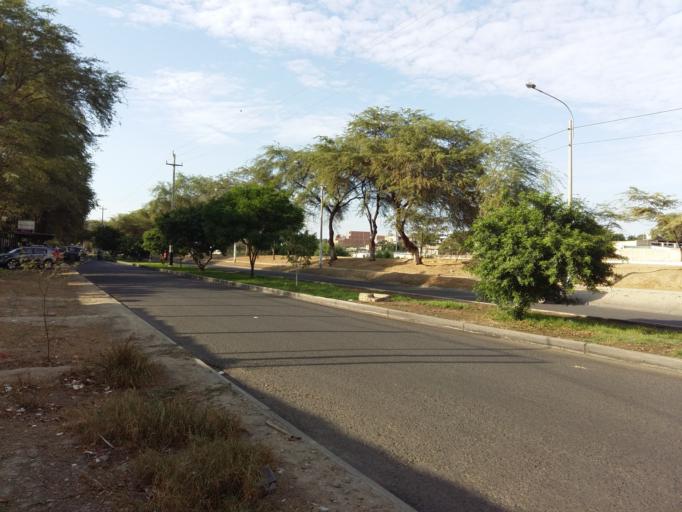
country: PE
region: Piura
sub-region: Provincia de Piura
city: Piura
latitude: -5.1860
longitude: -80.6236
